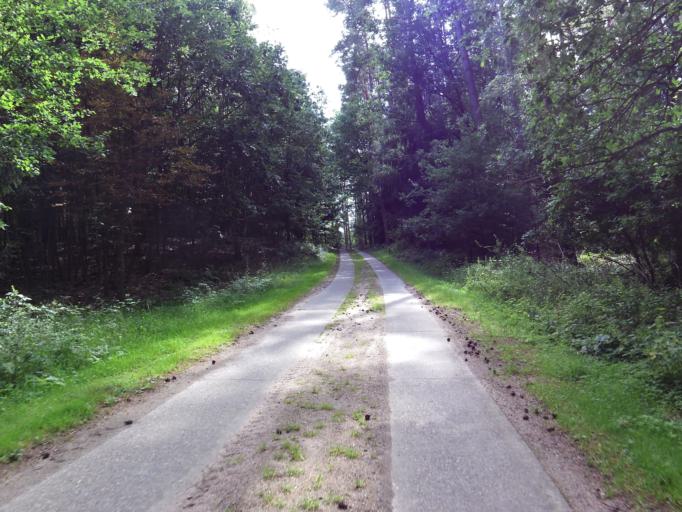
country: DE
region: Brandenburg
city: Lychen
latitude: 53.2814
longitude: 13.3659
